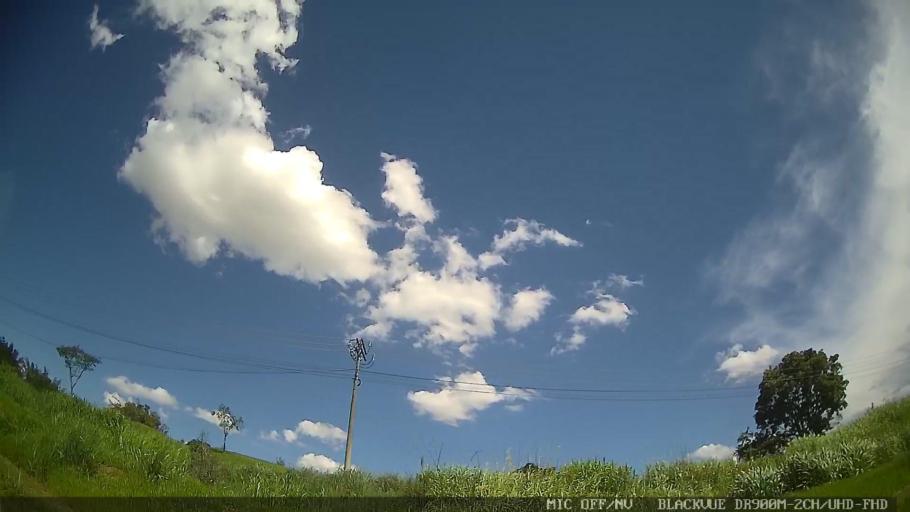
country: BR
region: Sao Paulo
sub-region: Pedreira
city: Pedreira
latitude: -22.7163
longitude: -46.8402
